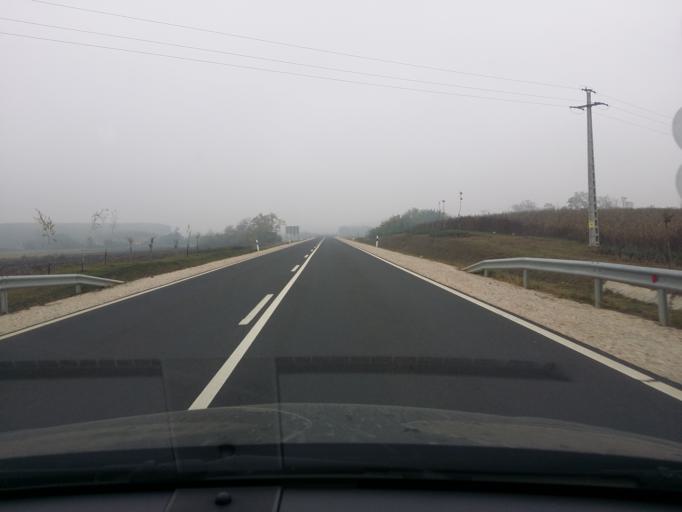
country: HU
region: Szabolcs-Szatmar-Bereg
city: Kalmanhaza
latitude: 47.9191
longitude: 21.6455
